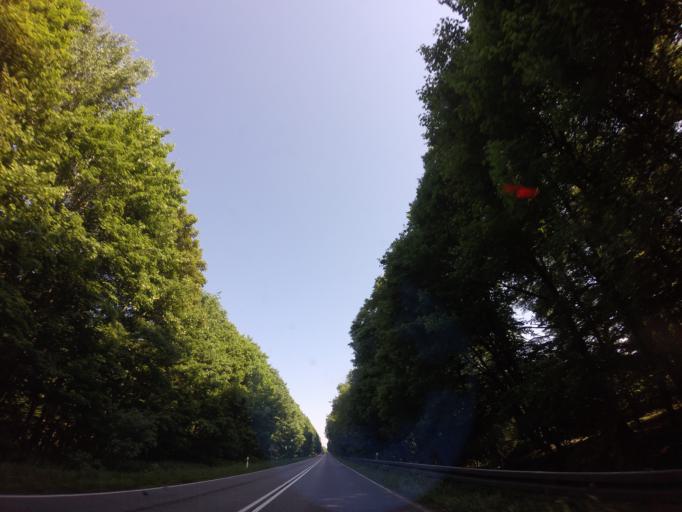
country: PL
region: West Pomeranian Voivodeship
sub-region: Powiat gryfinski
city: Stare Czarnowo
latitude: 53.3339
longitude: 14.7723
